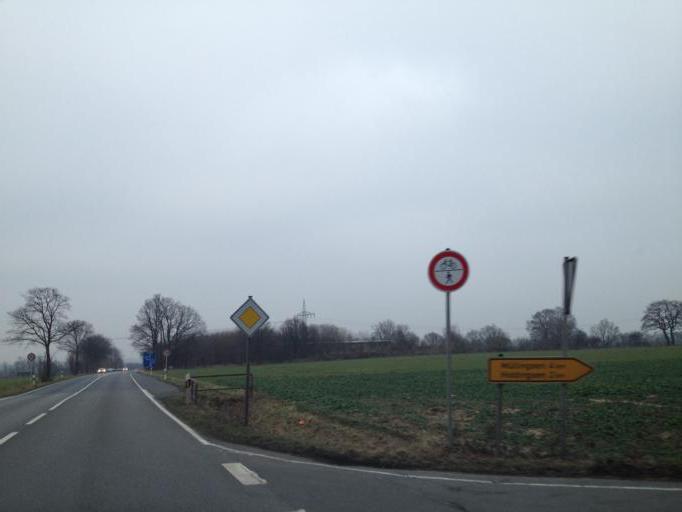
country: DE
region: North Rhine-Westphalia
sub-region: Regierungsbezirk Arnsberg
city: Soest
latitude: 51.5399
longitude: 8.0987
